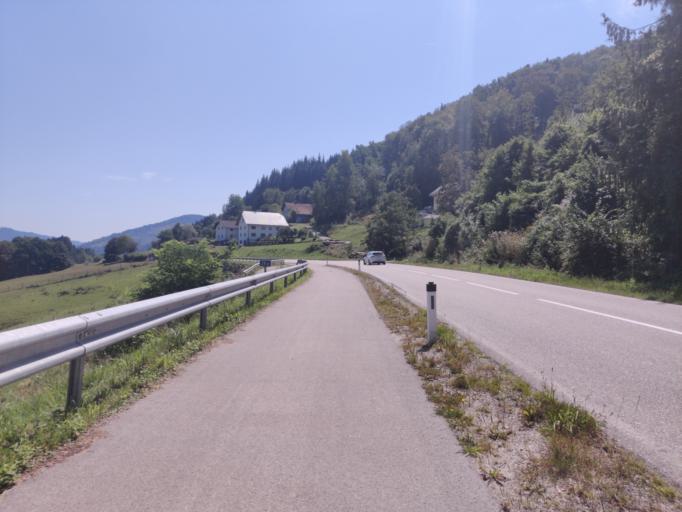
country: AT
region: Upper Austria
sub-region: Politischer Bezirk Rohrbach
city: Pfarrkirchen im Muehlkreis
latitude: 48.4794
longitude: 13.7613
